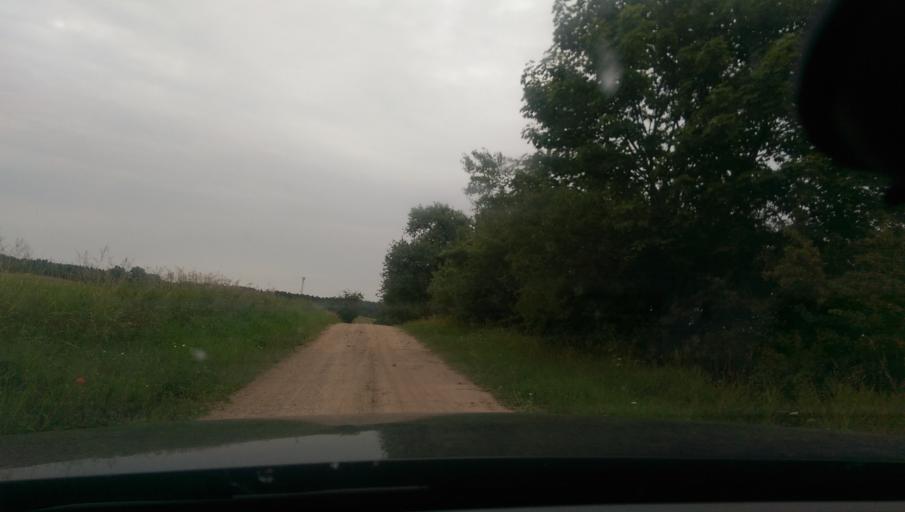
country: PL
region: Warmian-Masurian Voivodeship
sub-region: Powiat piski
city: Orzysz
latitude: 53.8181
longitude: 21.8055
